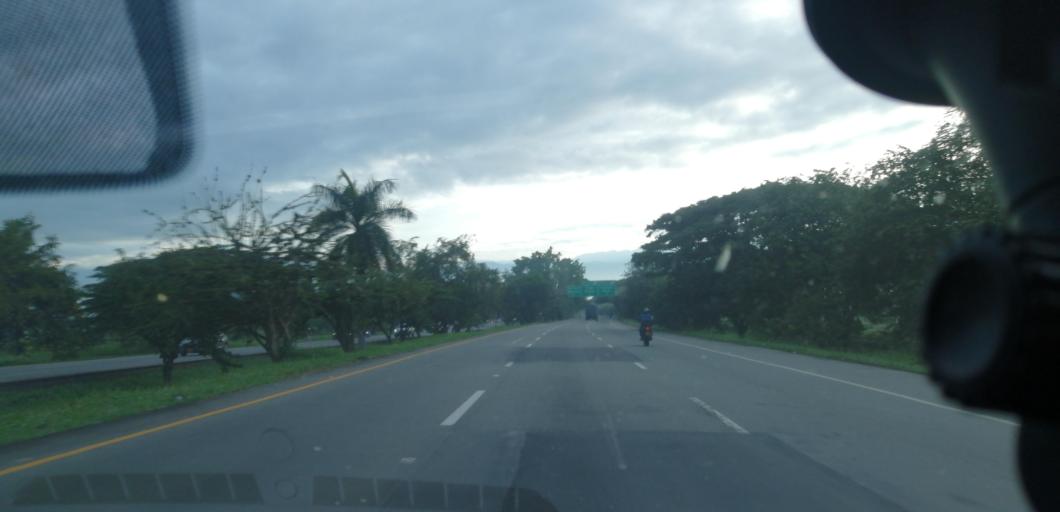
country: CO
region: Valle del Cauca
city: Palmira
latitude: 3.5226
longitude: -76.3463
